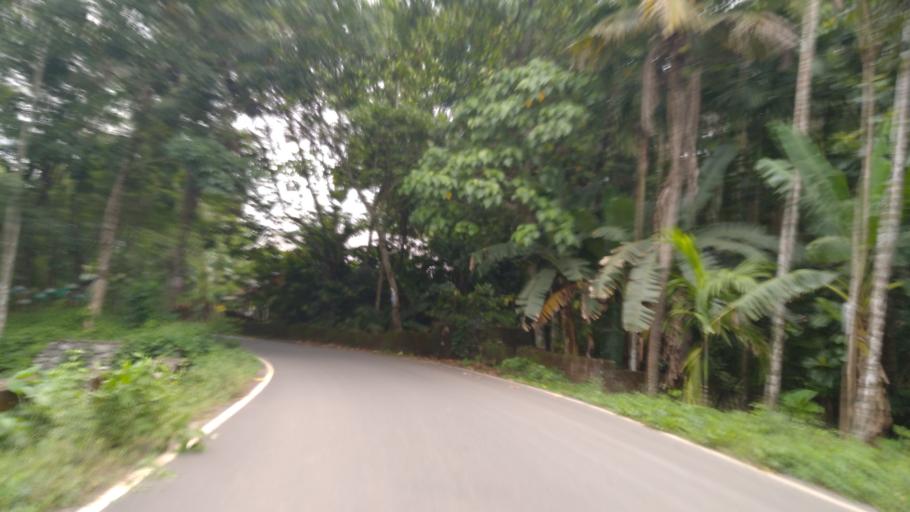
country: IN
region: Kerala
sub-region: Ernakulam
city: Perumbavoor
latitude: 10.0270
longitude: 76.4913
